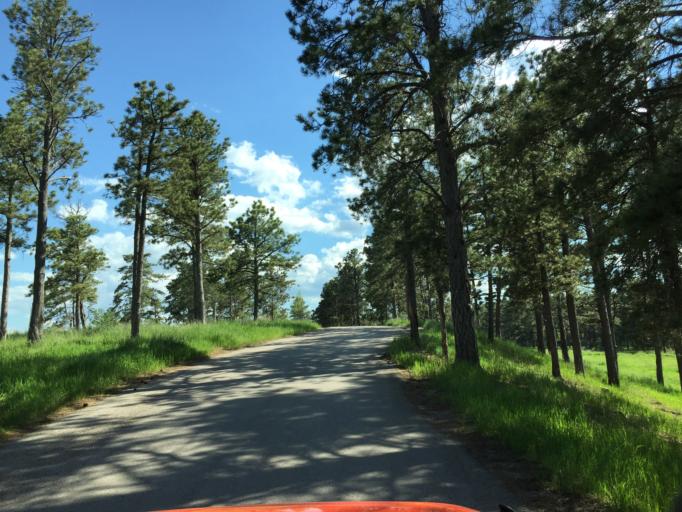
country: US
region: South Dakota
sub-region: Pennington County
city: Colonial Pine Hills
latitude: 43.9774
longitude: -103.3027
